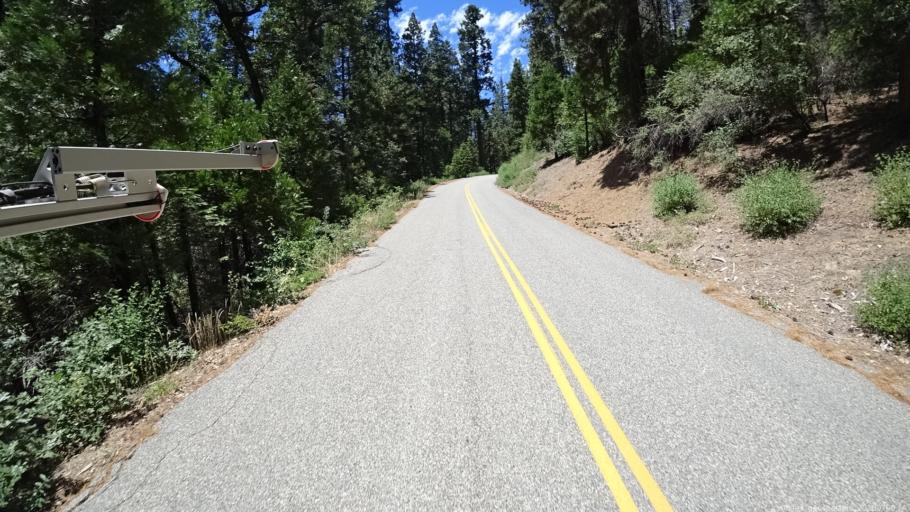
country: US
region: California
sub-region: Madera County
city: Oakhurst
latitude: 37.3710
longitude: -119.5365
